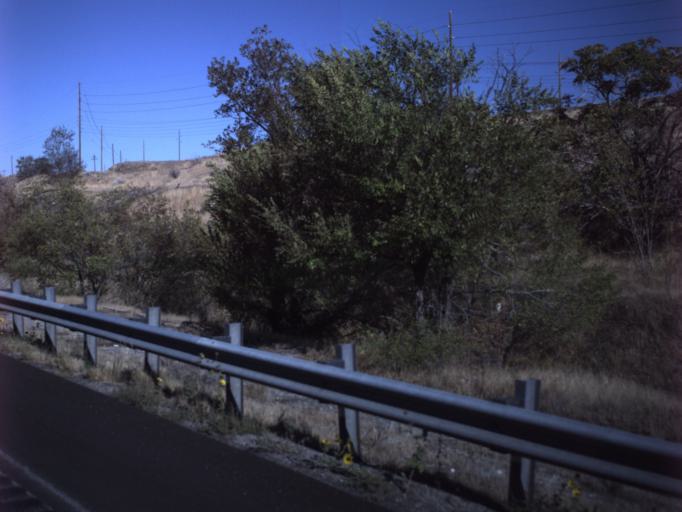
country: US
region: Utah
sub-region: Salt Lake County
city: Magna
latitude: 40.7179
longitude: -112.1376
